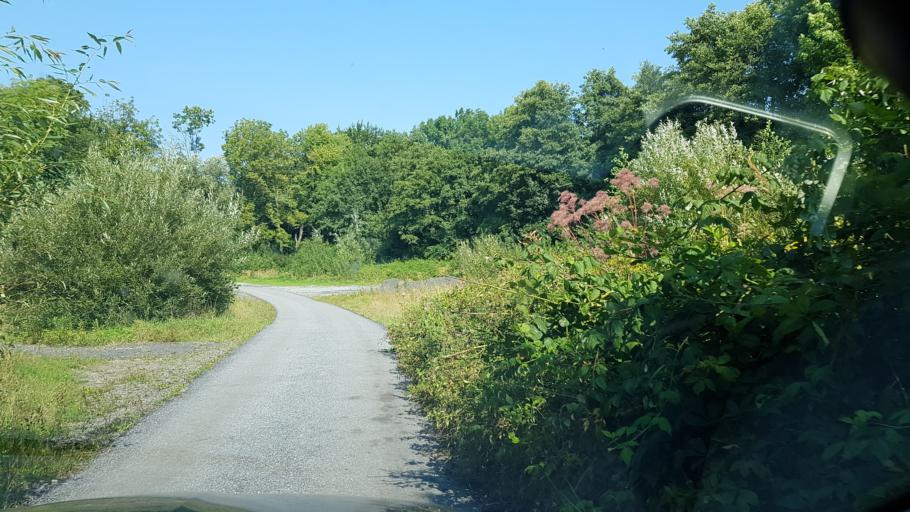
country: CZ
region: Olomoucky
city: Ceska Ves
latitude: 50.2697
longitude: 17.2345
